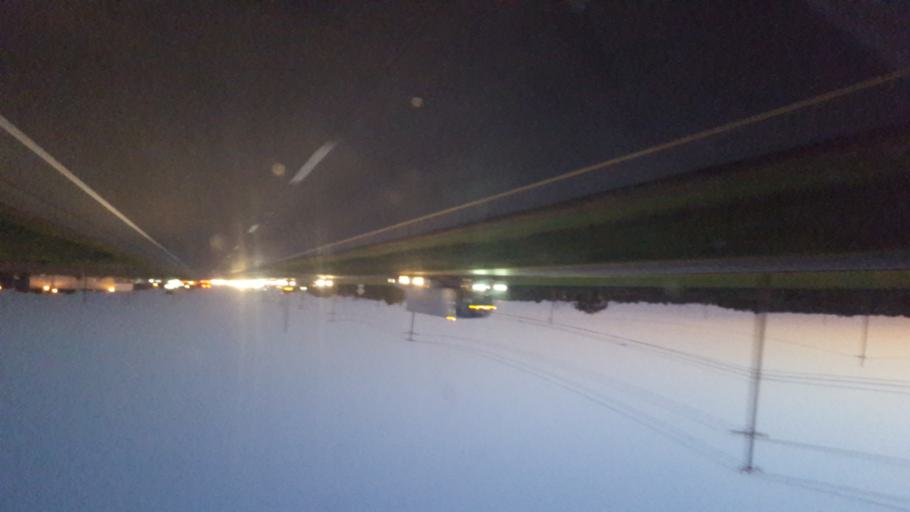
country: US
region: Ohio
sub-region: Pickaway County
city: Logan Elm Village
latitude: 39.5592
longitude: -82.9579
